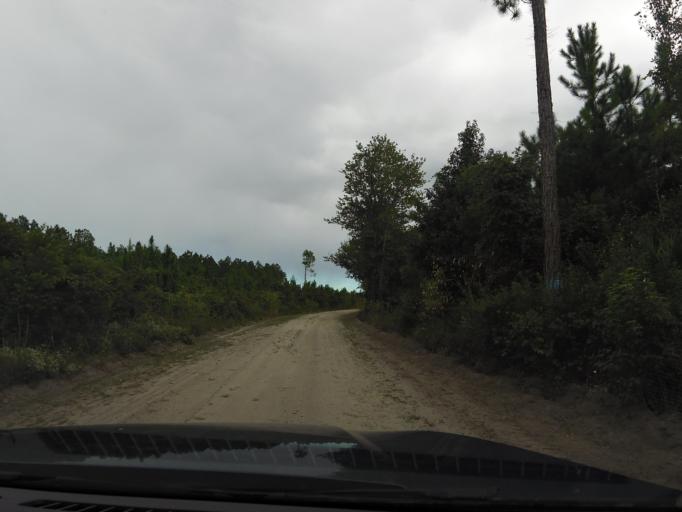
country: US
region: Florida
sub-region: Flagler County
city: Palm Coast
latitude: 29.5863
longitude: -81.3464
